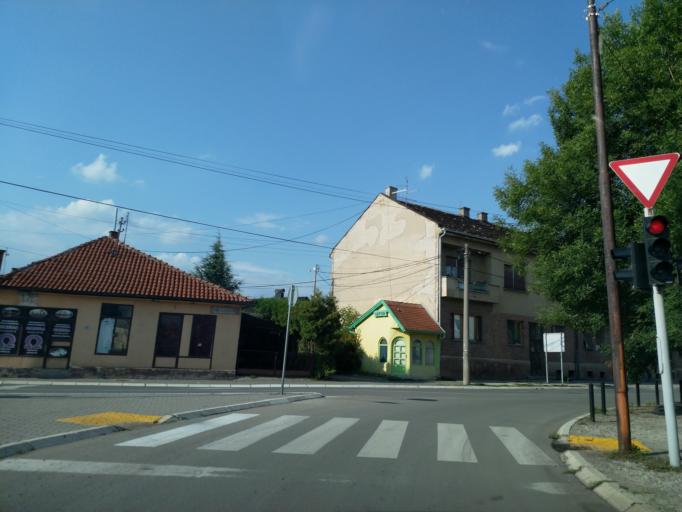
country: RS
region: Central Serbia
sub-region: Pomoravski Okrug
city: Paracin
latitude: 43.8616
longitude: 21.4060
